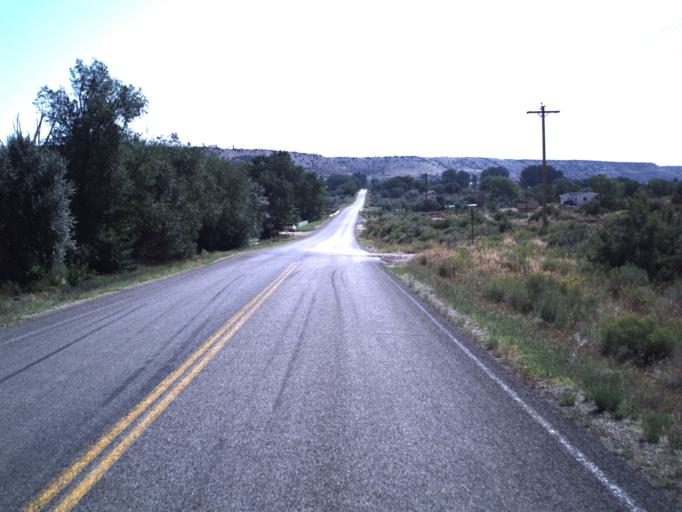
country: US
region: Utah
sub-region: Duchesne County
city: Duchesne
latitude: 40.2707
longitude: -110.4468
